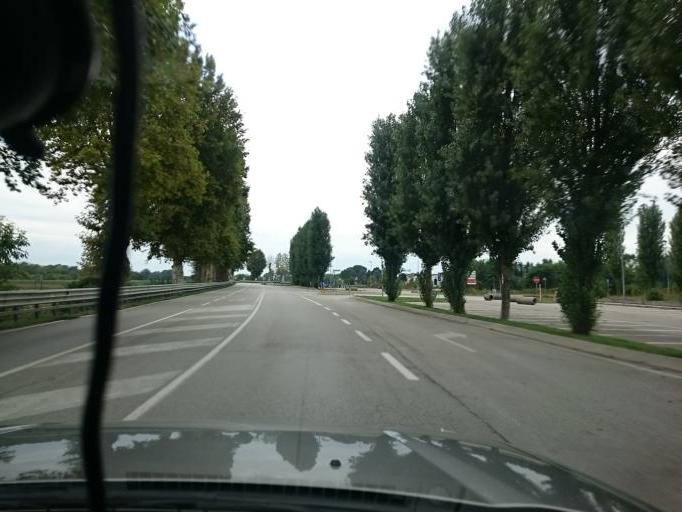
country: IT
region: Veneto
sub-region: Provincia di Padova
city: Arlesega
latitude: 45.4539
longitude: 11.7248
